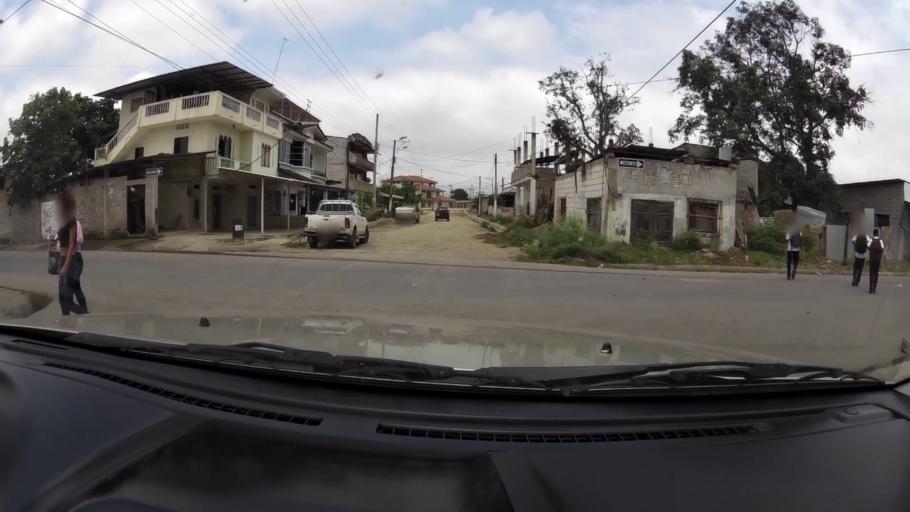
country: EC
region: El Oro
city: Pasaje
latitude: -3.2401
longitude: -79.8259
